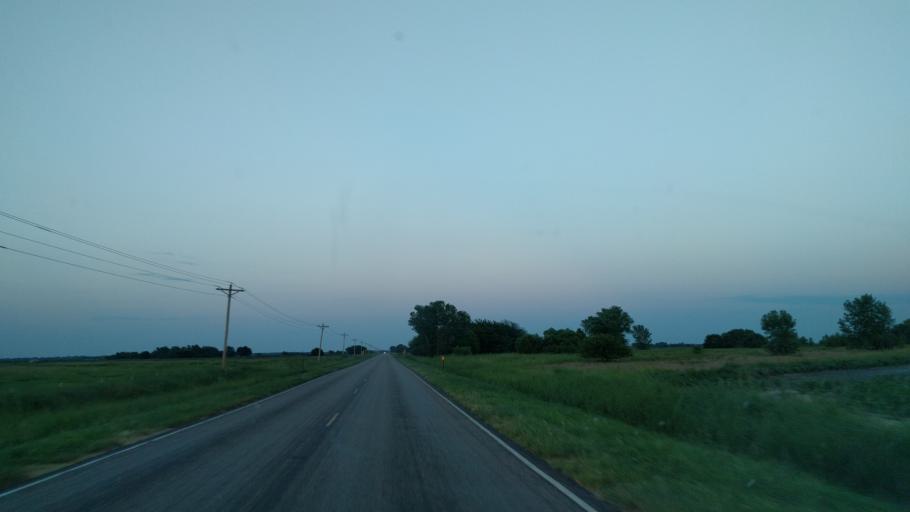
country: US
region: Kansas
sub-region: Reno County
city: Nickerson
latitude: 38.2176
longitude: -98.1229
